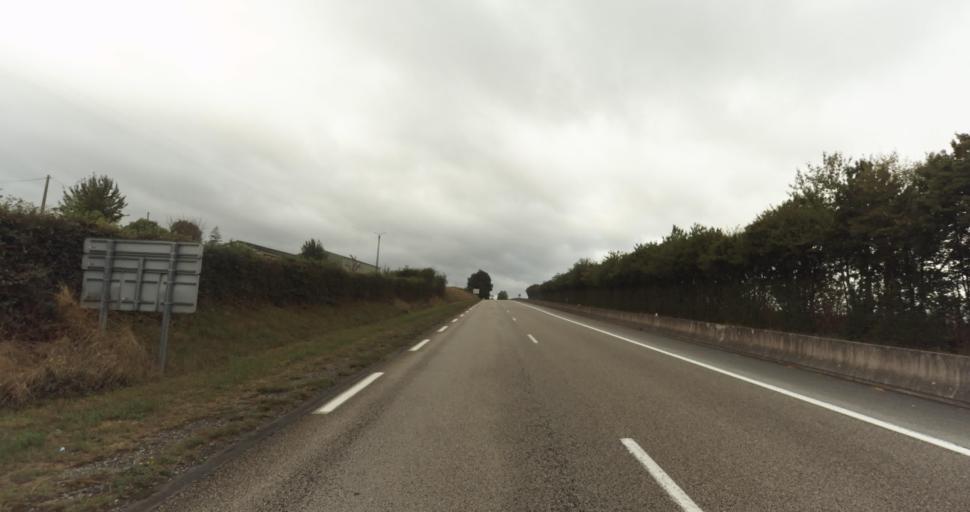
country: FR
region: Lower Normandy
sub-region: Departement de l'Orne
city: Sainte-Gauburge-Sainte-Colombe
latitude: 48.7267
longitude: 0.4705
